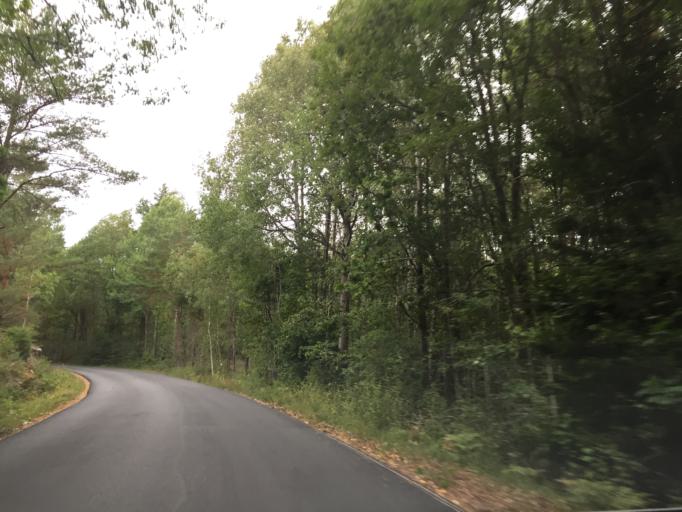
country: NO
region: Ostfold
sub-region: Hvaler
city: Skjaerhalden
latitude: 59.0709
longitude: 11.0294
